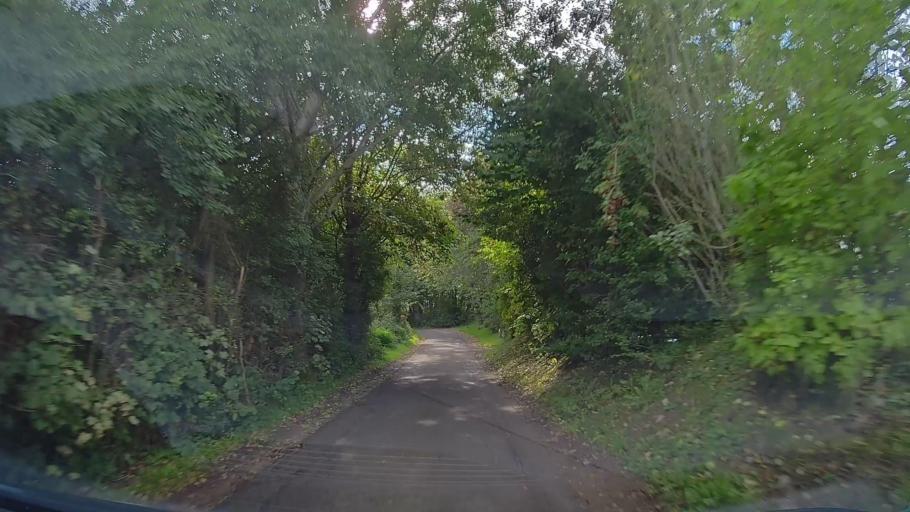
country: DE
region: Schleswig-Holstein
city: Ringsberg
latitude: 54.8292
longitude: 9.6042
